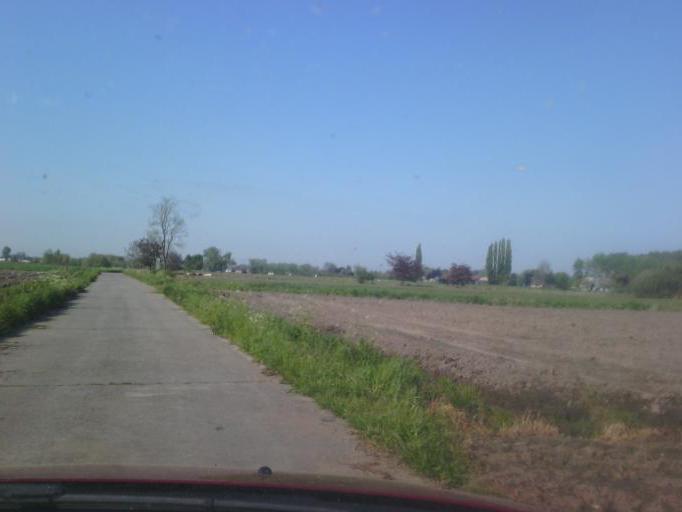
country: BE
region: Flanders
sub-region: Provincie Oost-Vlaanderen
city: Lokeren
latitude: 51.0667
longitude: 3.9408
